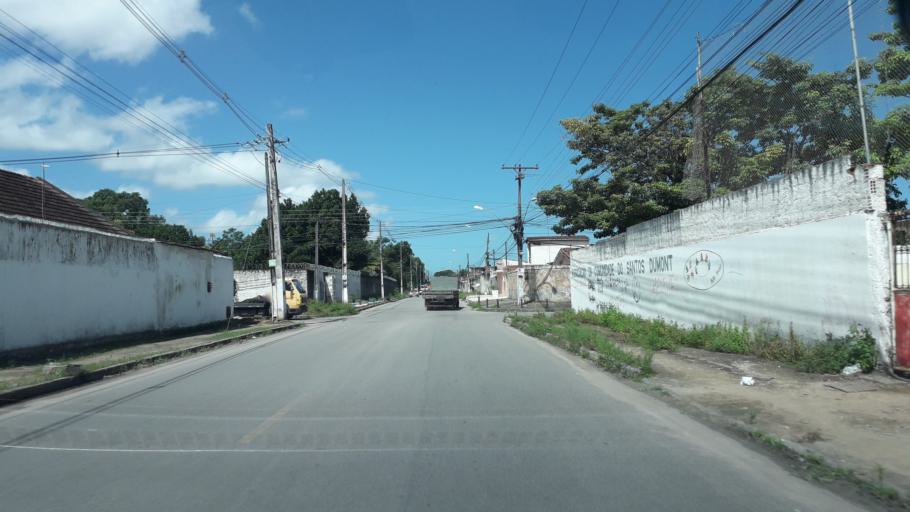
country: BR
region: Alagoas
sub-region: Satuba
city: Satuba
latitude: -9.5576
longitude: -35.7838
